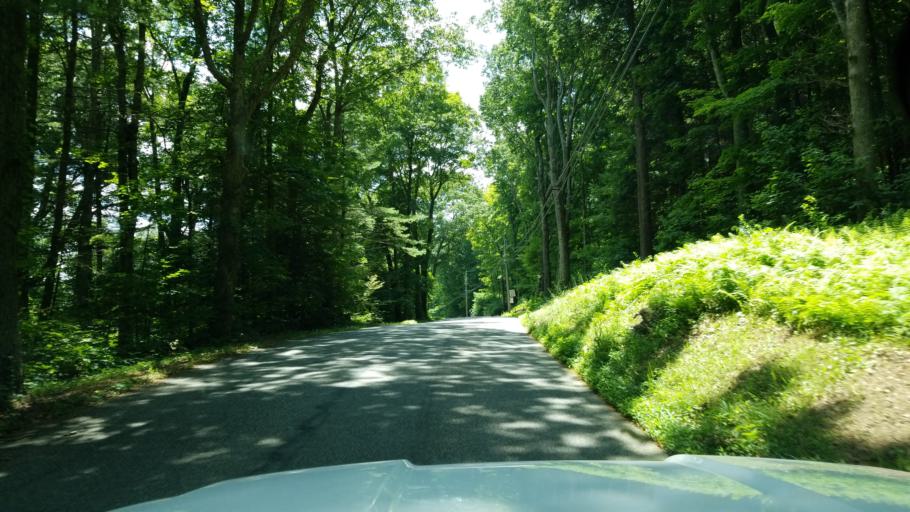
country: US
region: Massachusetts
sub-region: Hampden County
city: Holland
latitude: 41.9801
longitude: -72.1910
